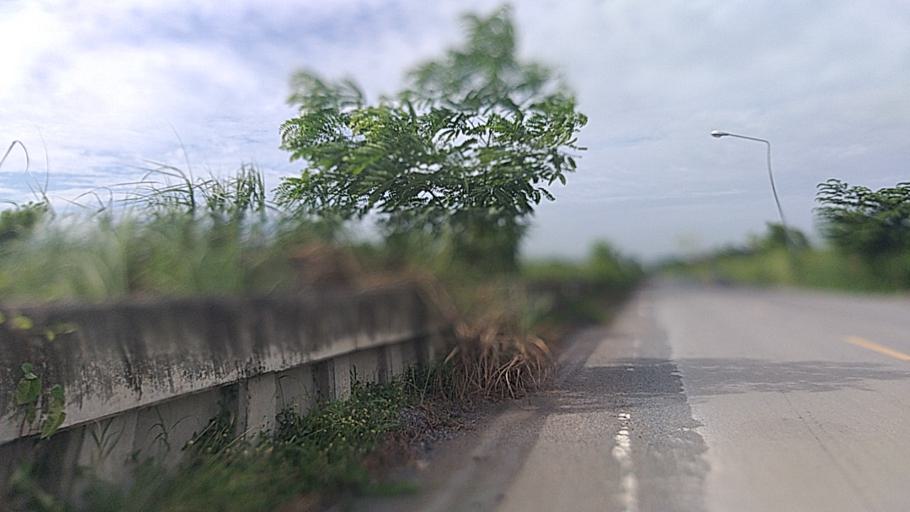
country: TH
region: Pathum Thani
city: Nong Suea
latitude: 14.0642
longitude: 100.8924
